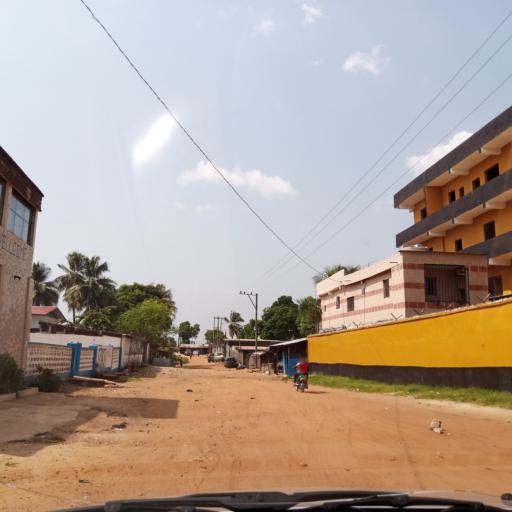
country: LR
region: Montserrado
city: Monrovia
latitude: 6.2898
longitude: -10.7648
